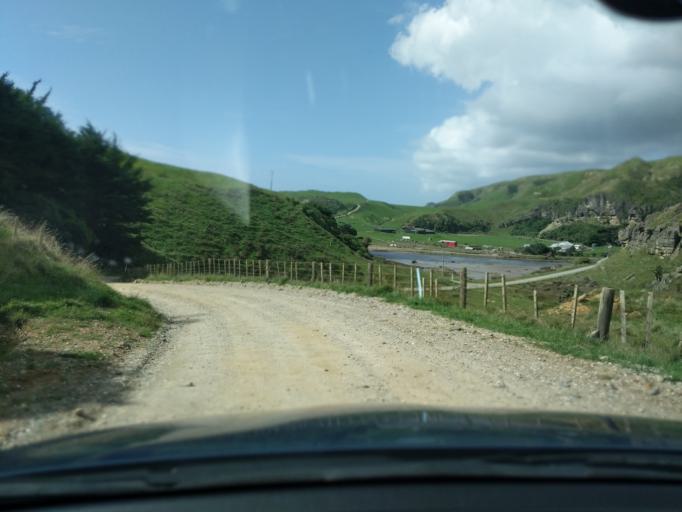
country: NZ
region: Tasman
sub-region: Tasman District
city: Takaka
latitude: -40.6469
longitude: 172.4293
